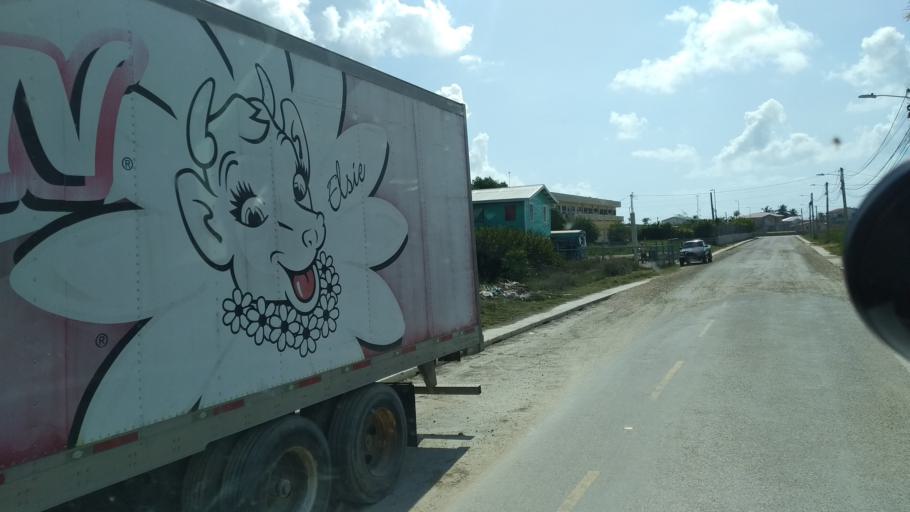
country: BZ
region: Belize
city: Belize City
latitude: 17.5149
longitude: -88.2294
